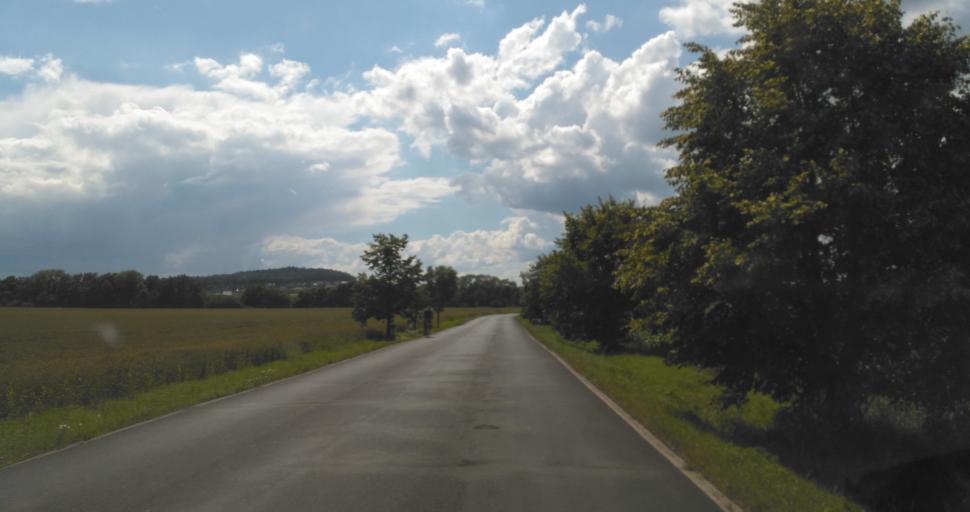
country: CZ
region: Central Bohemia
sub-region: Okres Beroun
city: Horovice
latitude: 49.8418
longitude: 13.9391
